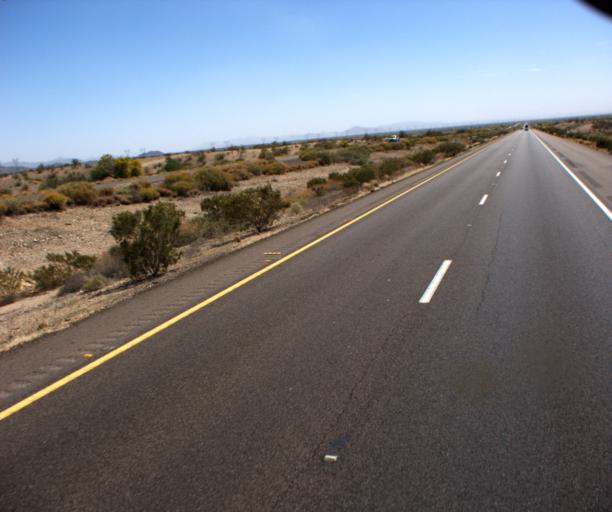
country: US
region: Arizona
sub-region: Maricopa County
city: Gila Bend
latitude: 33.0911
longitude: -112.6486
